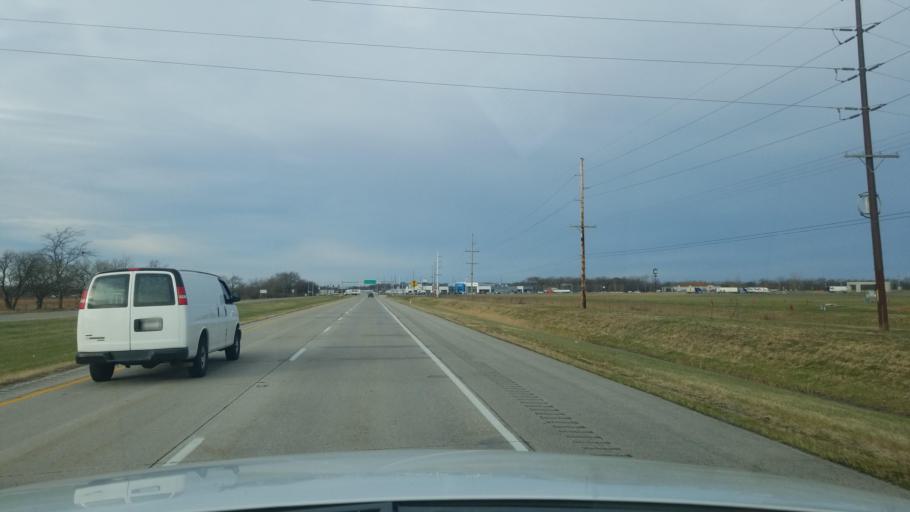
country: US
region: Indiana
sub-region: Posey County
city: Mount Vernon
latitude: 37.9430
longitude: -87.8450
